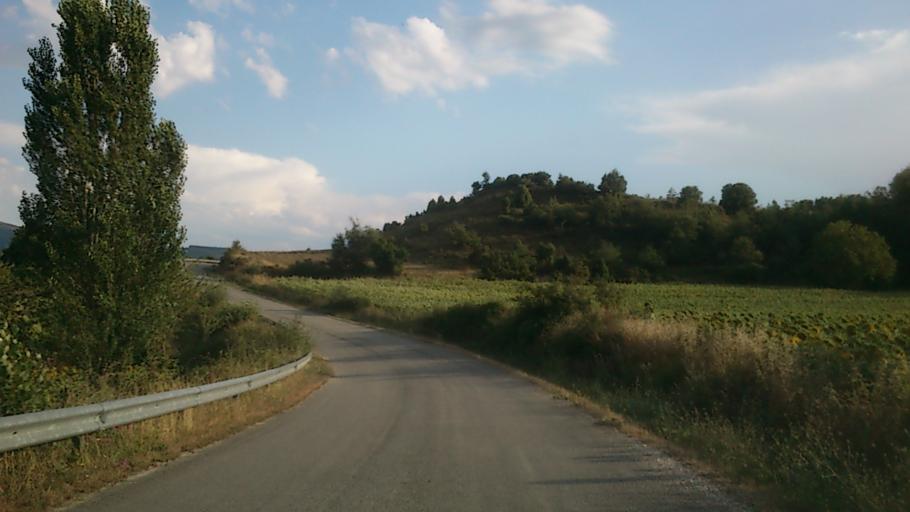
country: ES
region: Castille and Leon
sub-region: Provincia de Burgos
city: Frias
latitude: 42.8071
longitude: -3.2543
